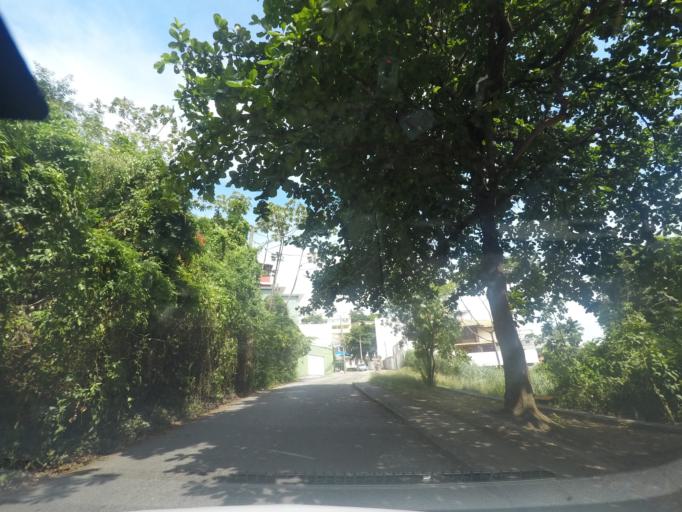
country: BR
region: Rio de Janeiro
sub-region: Rio De Janeiro
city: Rio de Janeiro
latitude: -22.8147
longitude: -43.1971
